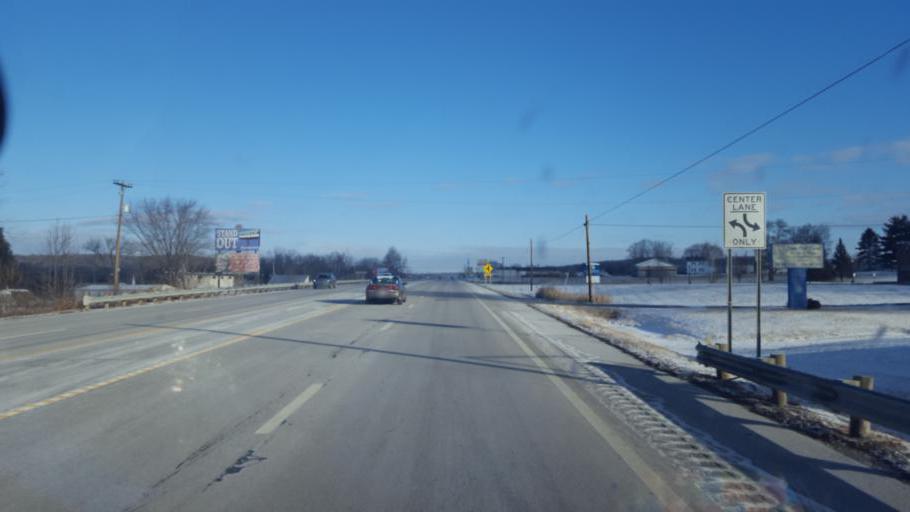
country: US
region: Ohio
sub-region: Pike County
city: Waverly
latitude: 39.1437
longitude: -82.9774
